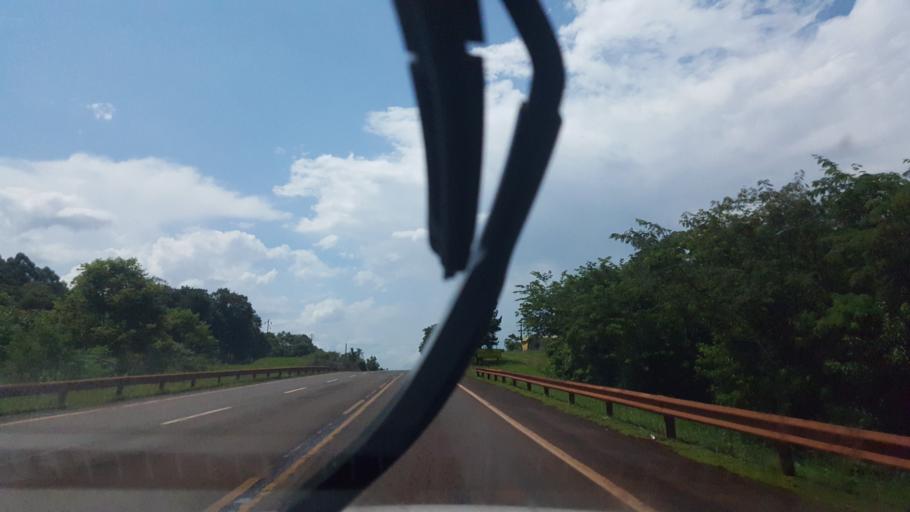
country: AR
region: Misiones
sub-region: Departamento de Eldorado
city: Eldorado
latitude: -26.3722
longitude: -54.6245
